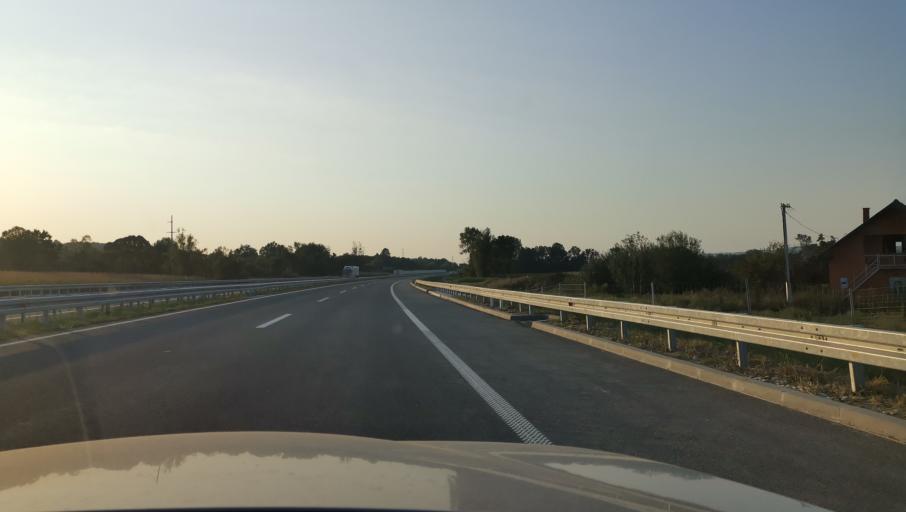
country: RS
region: Central Serbia
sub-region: Kolubarski Okrug
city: Ljig
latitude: 44.2907
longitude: 20.2409
